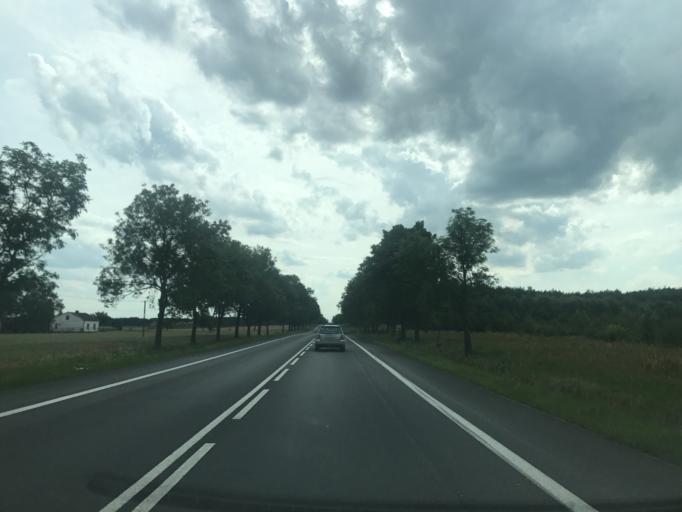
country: PL
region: Masovian Voivodeship
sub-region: Powiat mlawski
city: Strzegowo
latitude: 52.9713
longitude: 20.3091
